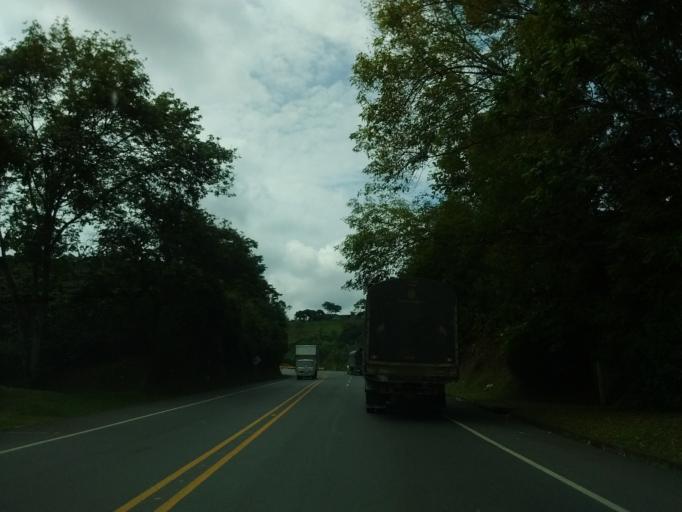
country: CO
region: Cauca
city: Morales
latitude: 2.7252
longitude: -76.5447
